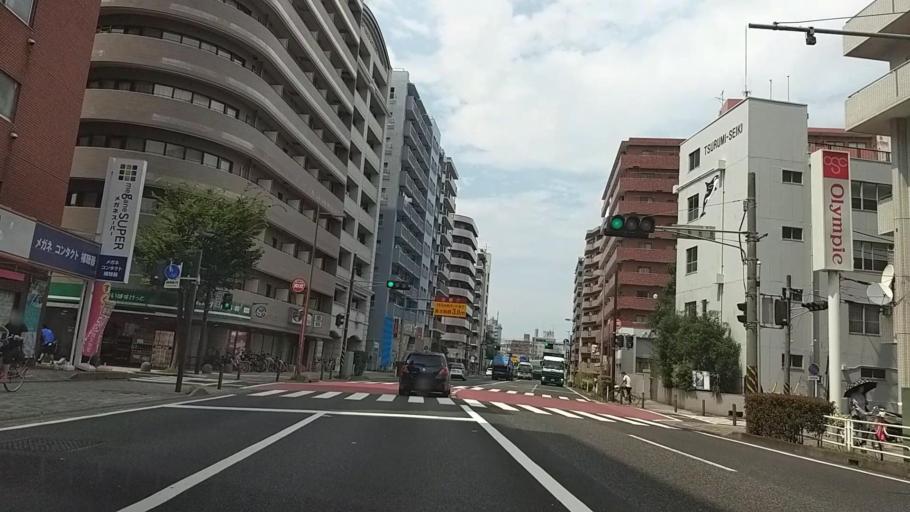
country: JP
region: Kanagawa
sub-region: Kawasaki-shi
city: Kawasaki
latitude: 35.5100
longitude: 139.6793
